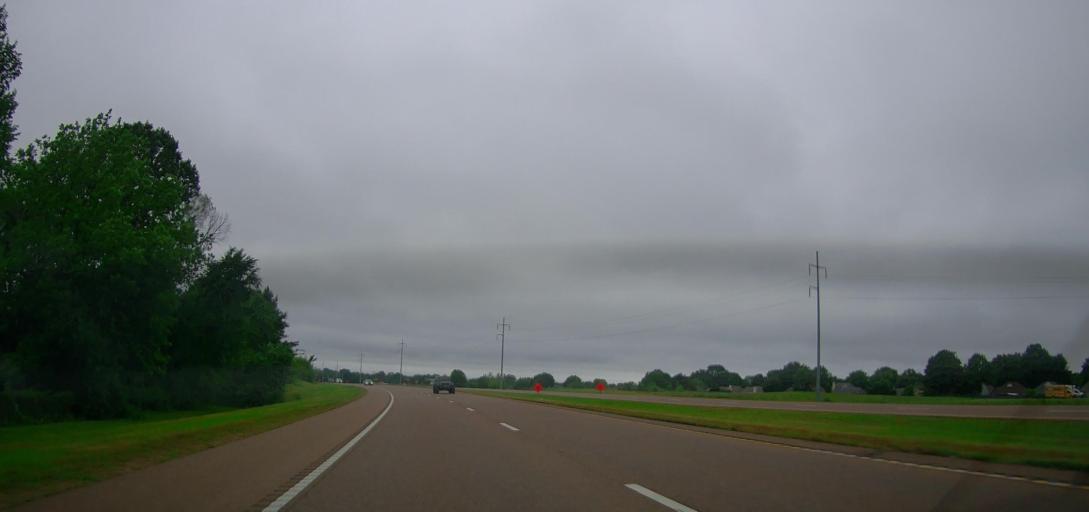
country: US
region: Mississippi
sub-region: De Soto County
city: Olive Branch
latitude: 34.9687
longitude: -89.8071
